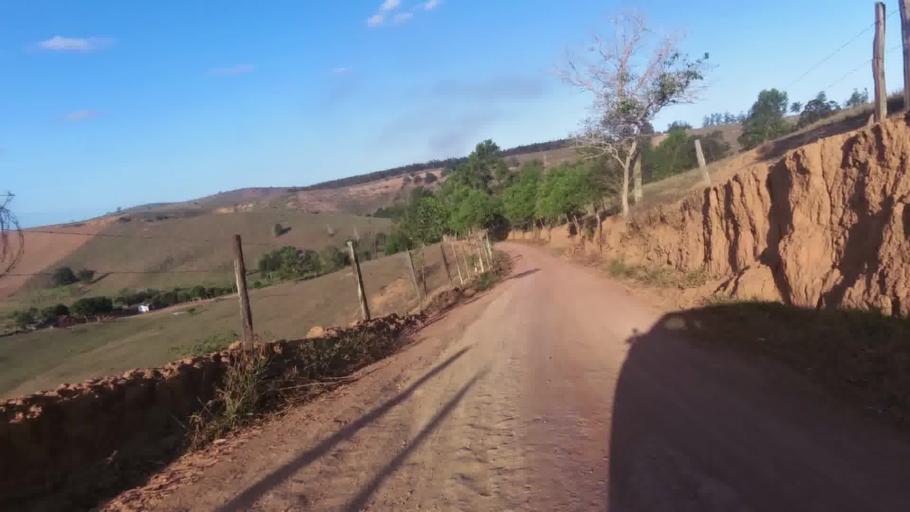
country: BR
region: Espirito Santo
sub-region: Marataizes
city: Marataizes
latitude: -21.1642
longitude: -41.0560
